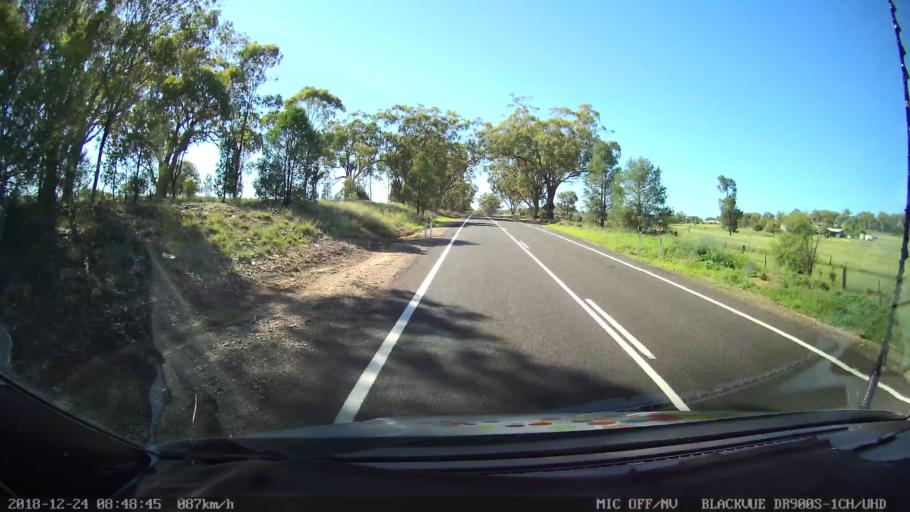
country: AU
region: New South Wales
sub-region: Liverpool Plains
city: Quirindi
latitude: -31.4595
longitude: 150.6481
